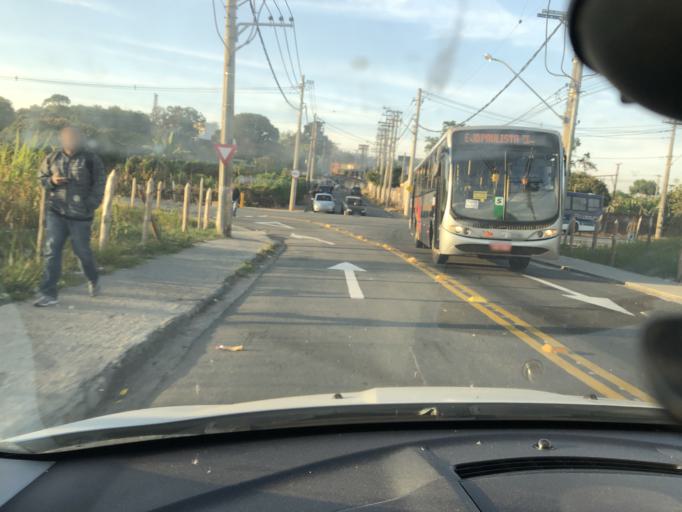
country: BR
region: Sao Paulo
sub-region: Varzea Paulista
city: Varzea Paulista
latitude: -23.2083
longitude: -46.8306
